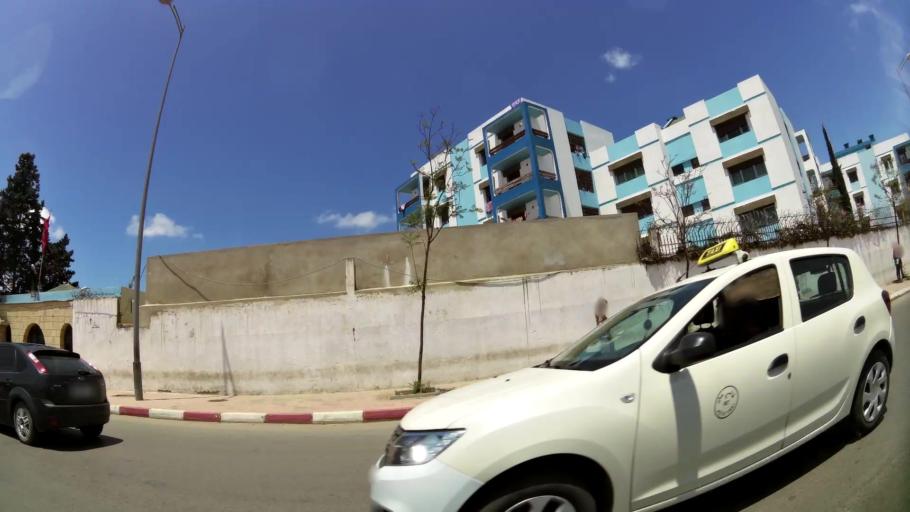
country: MA
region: Gharb-Chrarda-Beni Hssen
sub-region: Kenitra Province
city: Kenitra
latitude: 34.2491
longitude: -6.5570
